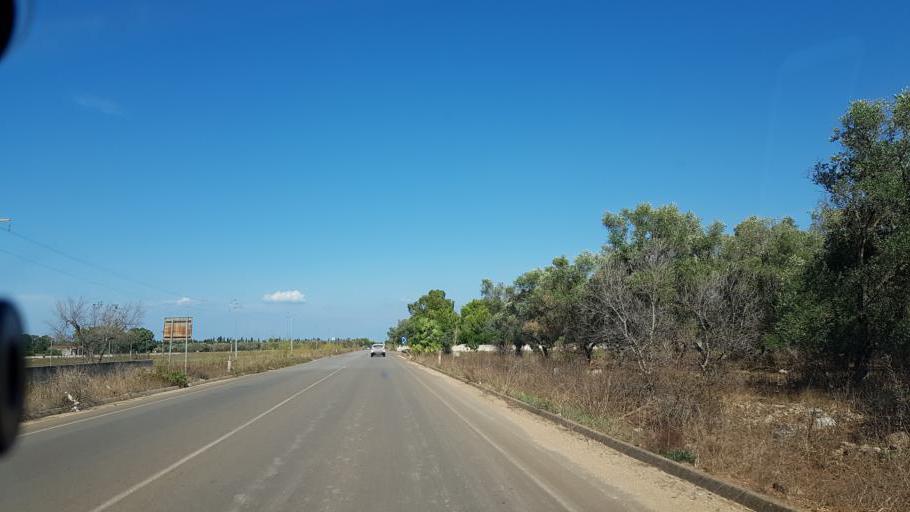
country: IT
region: Apulia
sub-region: Provincia di Lecce
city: Leverano
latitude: 40.2612
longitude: 18.0051
